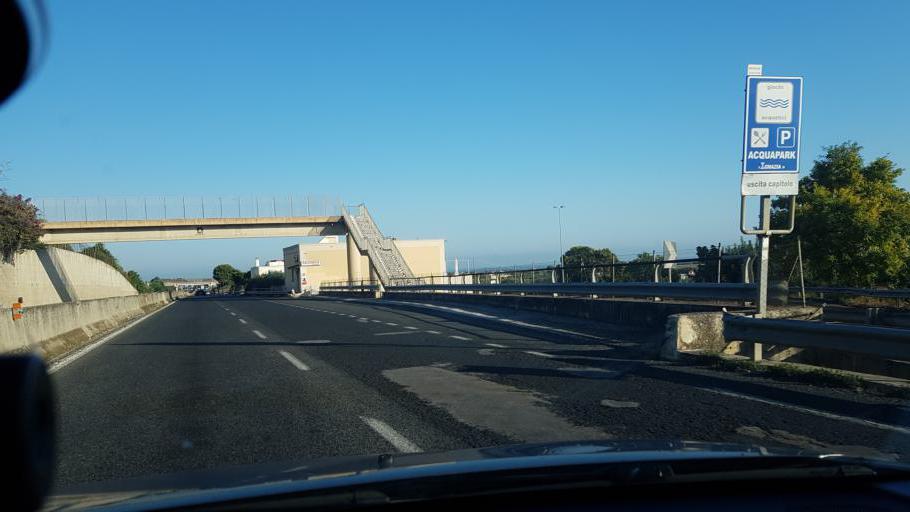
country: IT
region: Apulia
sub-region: Provincia di Brindisi
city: Fasano
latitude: 40.8898
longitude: 17.3334
